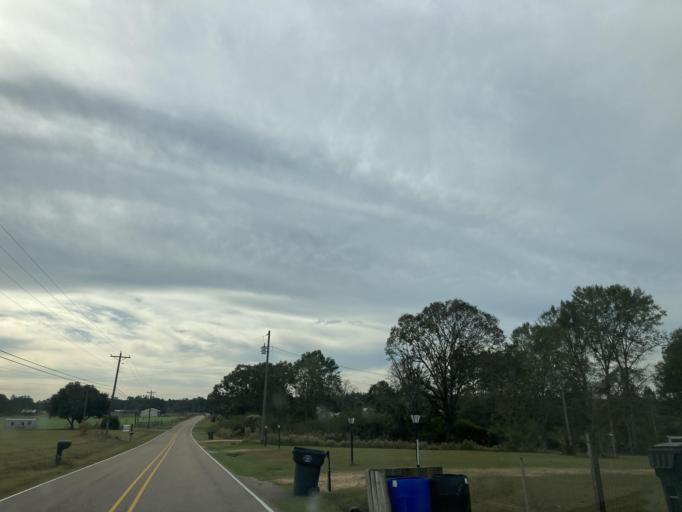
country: US
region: Mississippi
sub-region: Lamar County
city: Purvis
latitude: 31.1067
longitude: -89.4719
